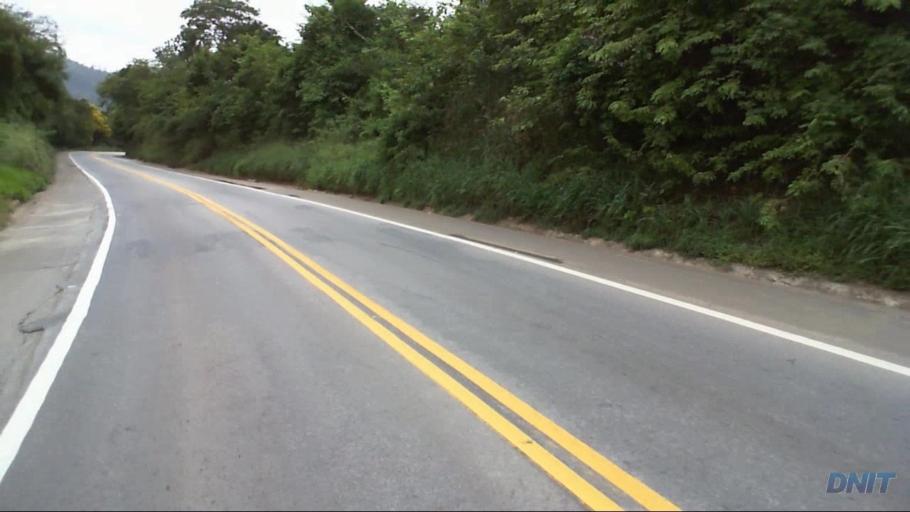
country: BR
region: Minas Gerais
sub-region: Timoteo
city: Timoteo
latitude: -19.5713
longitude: -42.7132
